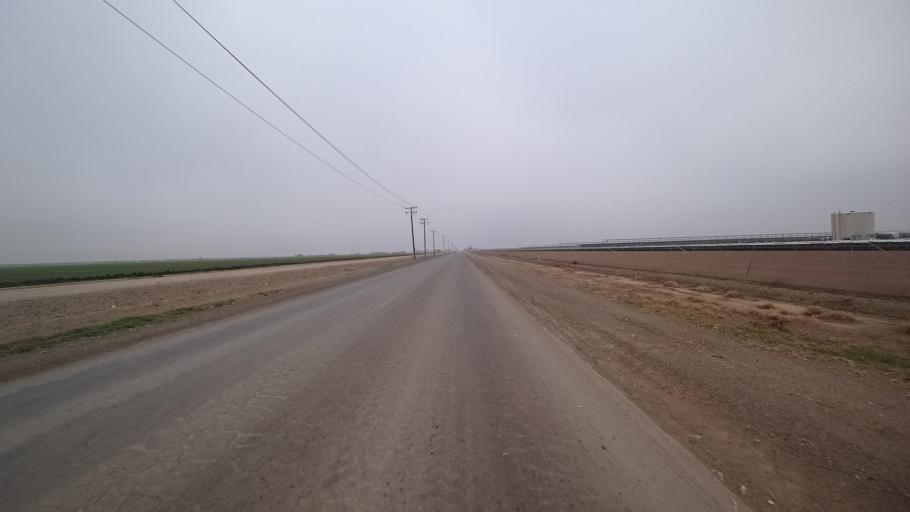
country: US
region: California
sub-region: Kern County
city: Rosedale
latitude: 35.2091
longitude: -119.1795
